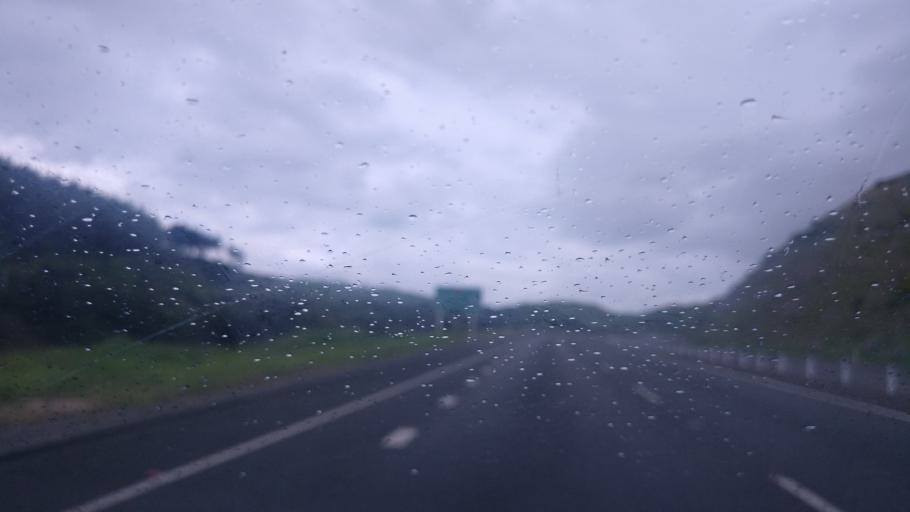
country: NZ
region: Wellington
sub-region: Porirua City
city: Porirua
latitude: -41.0728
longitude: 174.8753
